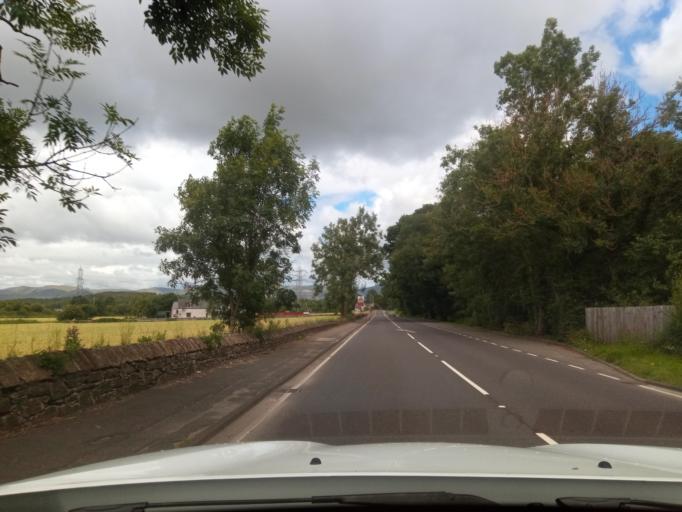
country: GB
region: Scotland
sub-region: Fife
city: Kincardine
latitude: 56.0823
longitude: -3.7203
